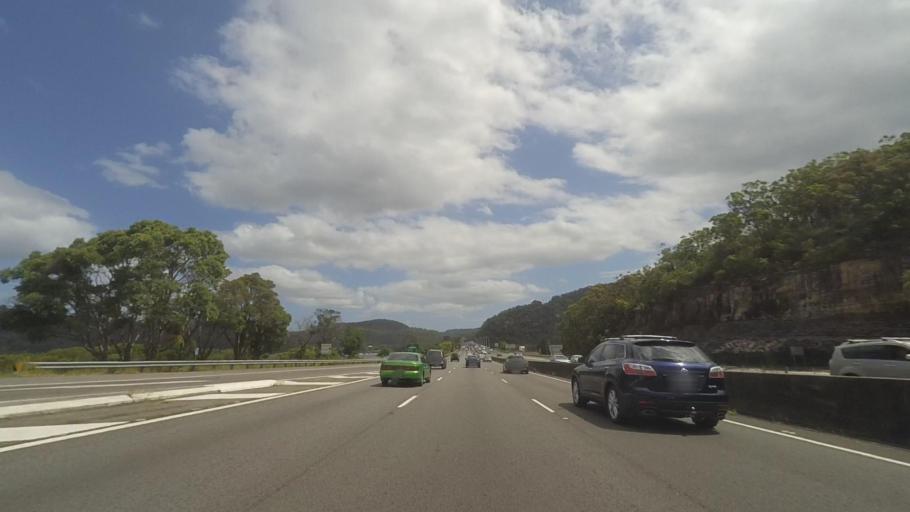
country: AU
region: New South Wales
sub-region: Hornsby Shire
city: Berowra
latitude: -33.5323
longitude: 151.2006
